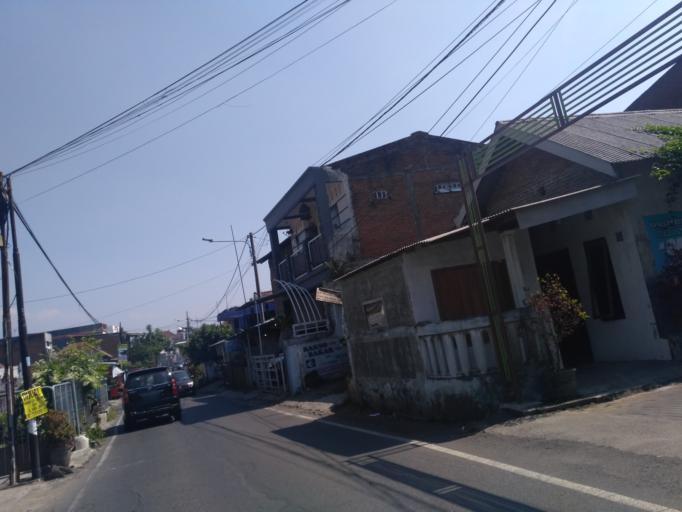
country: ID
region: East Java
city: Malang
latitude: -7.9348
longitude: 112.6159
